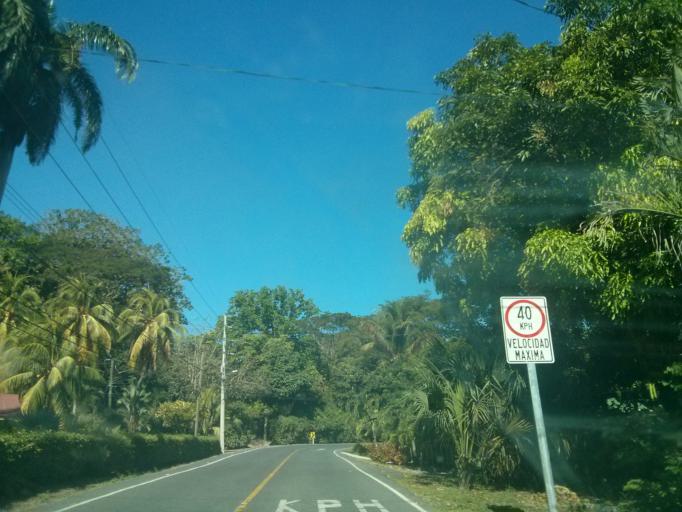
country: CR
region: Puntarenas
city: Paquera
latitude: 9.8068
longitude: -84.9436
